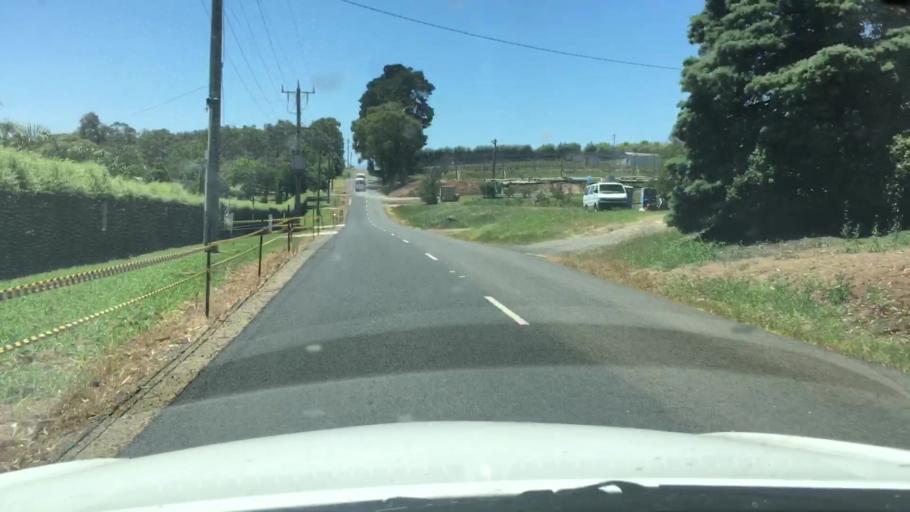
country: AU
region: Victoria
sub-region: Yarra Ranges
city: Mount Evelyn
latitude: -37.8000
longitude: 145.4475
